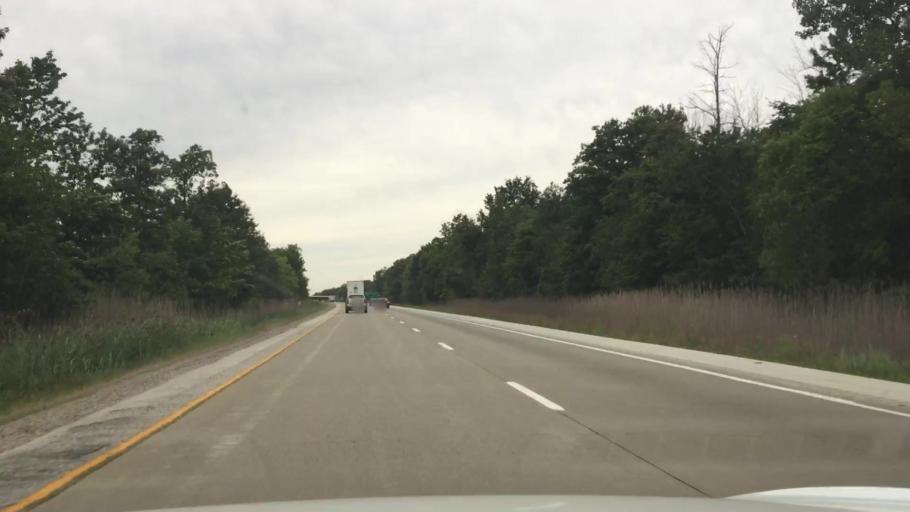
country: CA
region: Ontario
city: Camlachie
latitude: 42.9913
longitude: -82.1056
